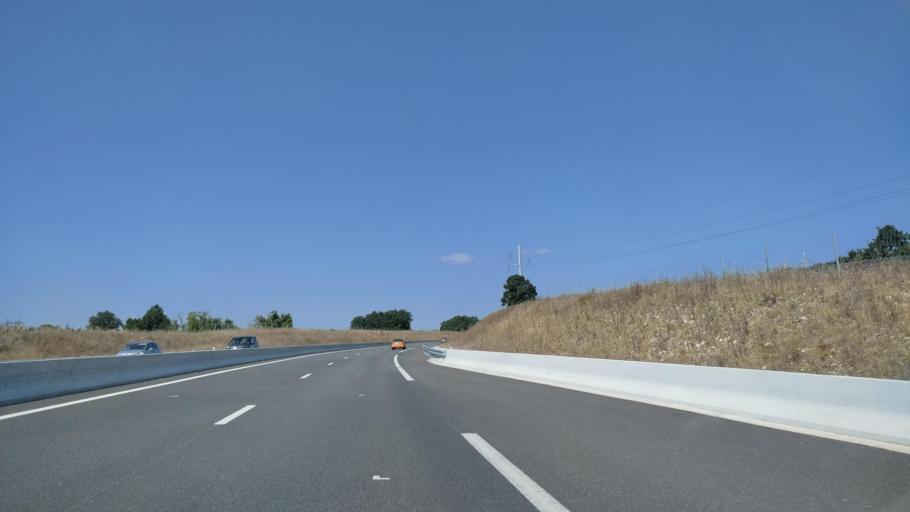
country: FR
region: Poitou-Charentes
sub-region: Departement de la Charente
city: Fleac
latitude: 45.6902
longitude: 0.0843
